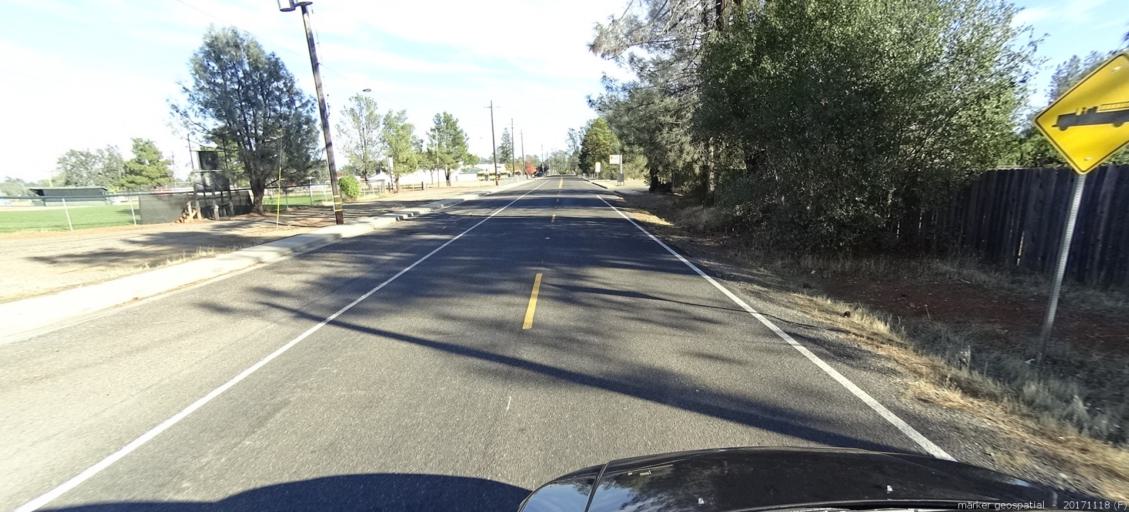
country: US
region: California
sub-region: Shasta County
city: Anderson
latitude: 40.4465
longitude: -122.4126
